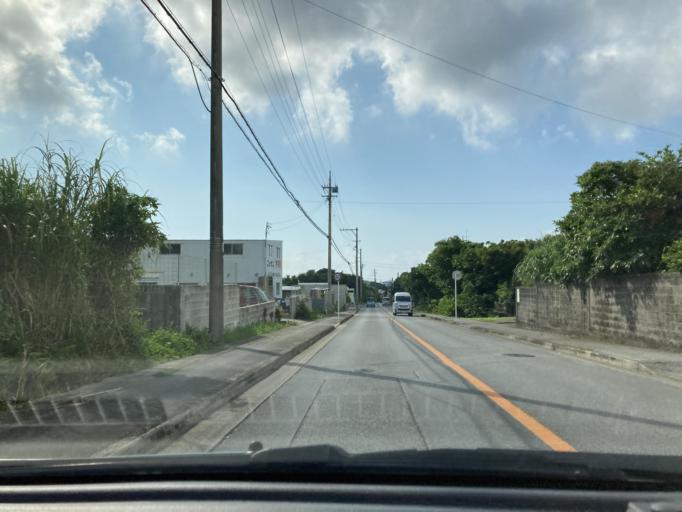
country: JP
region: Okinawa
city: Itoman
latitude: 26.1355
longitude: 127.7695
